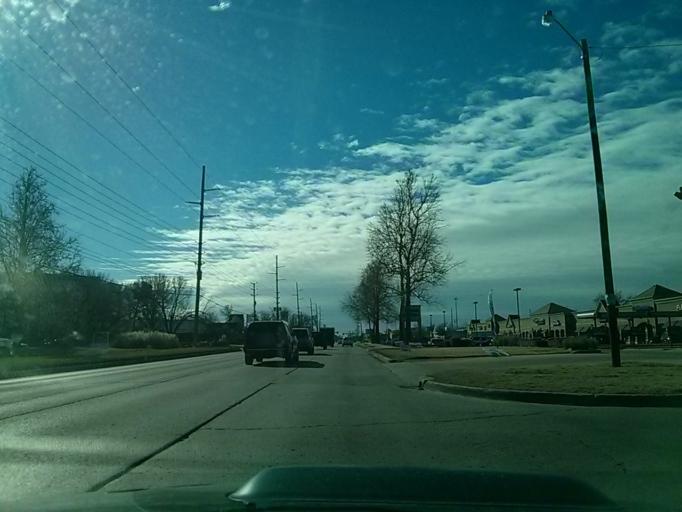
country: US
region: Oklahoma
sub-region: Tulsa County
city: Jenks
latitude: 36.0787
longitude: -95.9581
